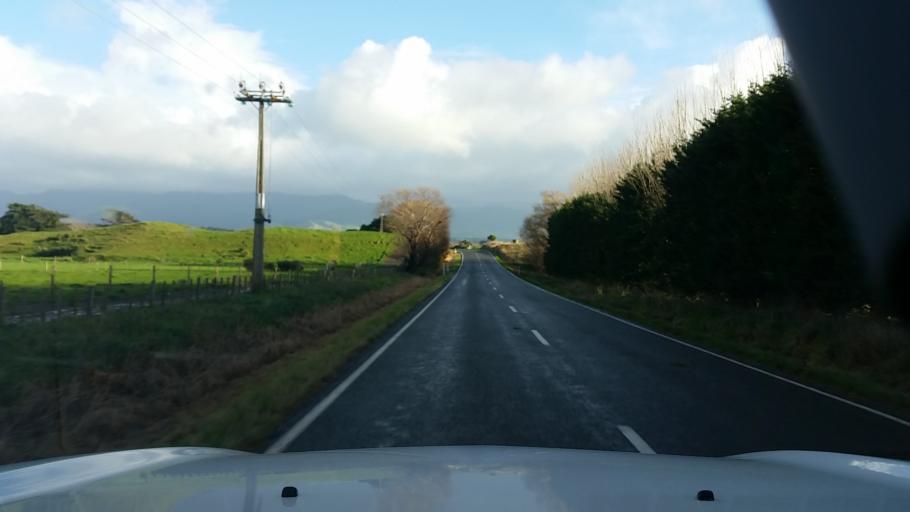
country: NZ
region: Wellington
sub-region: Upper Hutt City
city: Upper Hutt
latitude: -41.3281
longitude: 175.2308
